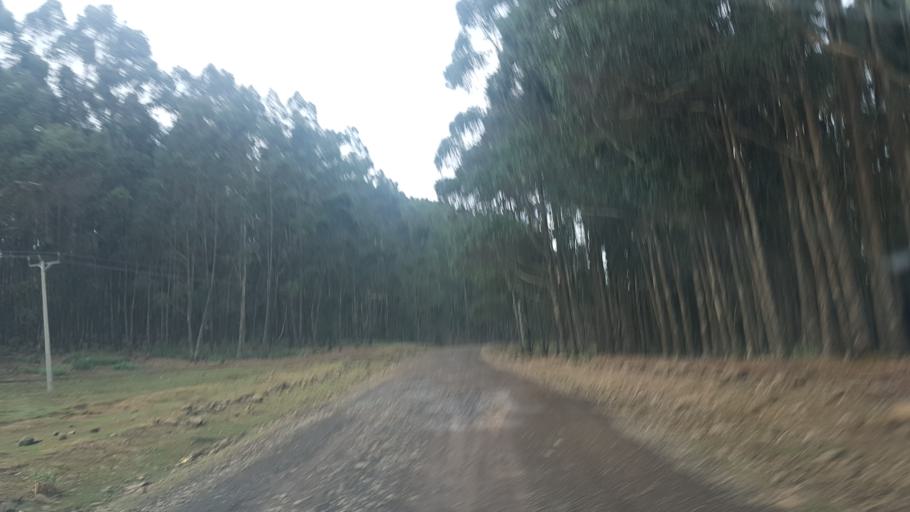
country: ET
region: Amhara
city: Finote Selam
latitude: 10.7945
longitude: 37.6634
